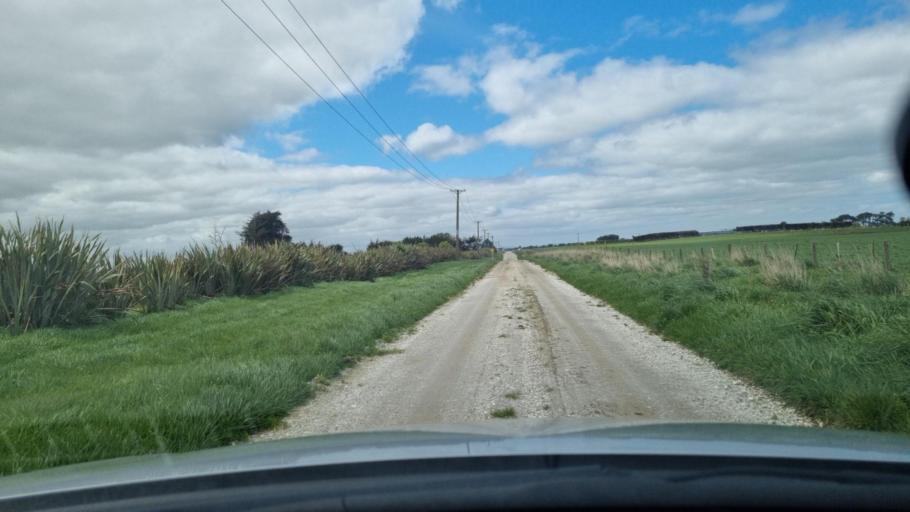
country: NZ
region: Southland
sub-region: Invercargill City
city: Invercargill
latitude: -46.4427
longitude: 168.4542
